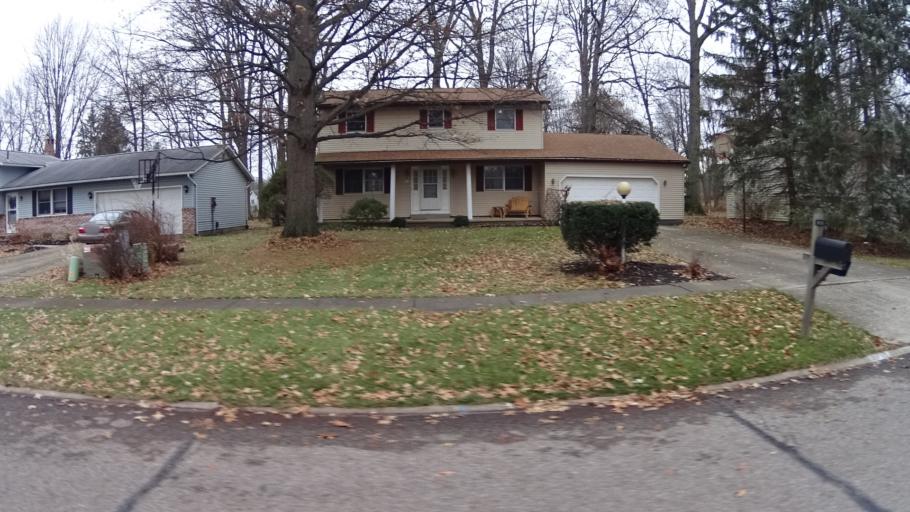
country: US
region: Ohio
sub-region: Lorain County
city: North Ridgeville
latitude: 41.3640
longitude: -81.9959
